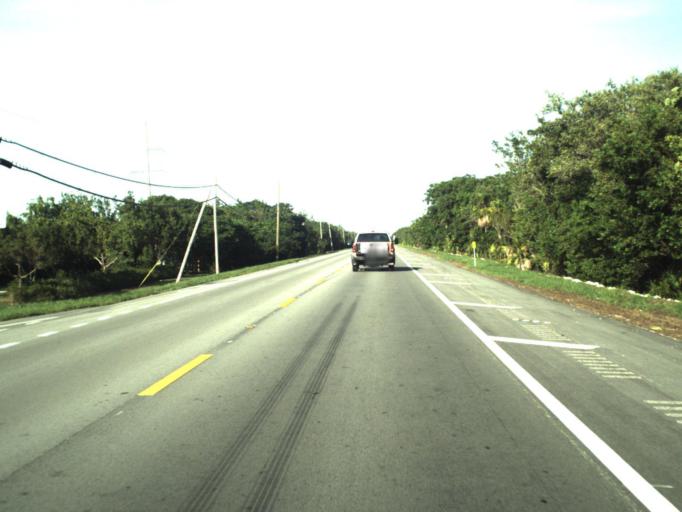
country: US
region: Florida
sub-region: Monroe County
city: Marathon
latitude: 24.7413
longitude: -80.9964
